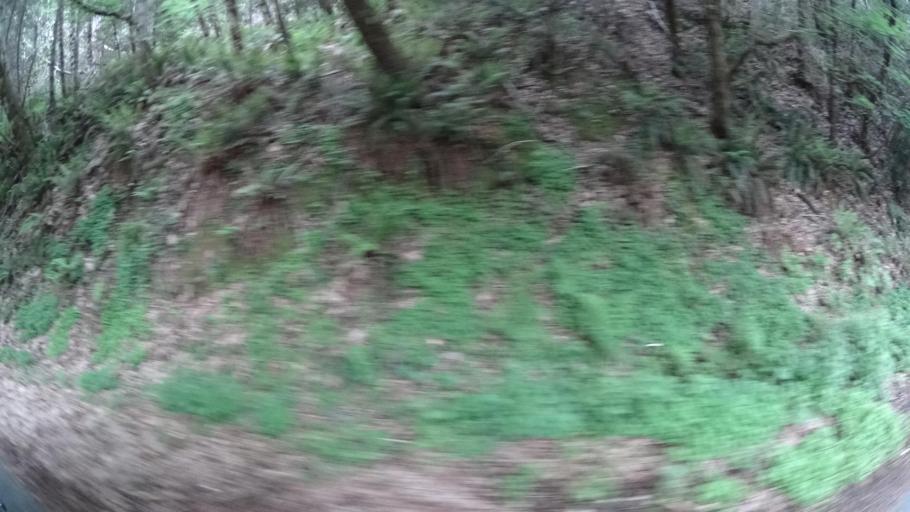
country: US
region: California
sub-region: Humboldt County
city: Willow Creek
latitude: 41.2045
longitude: -123.7563
